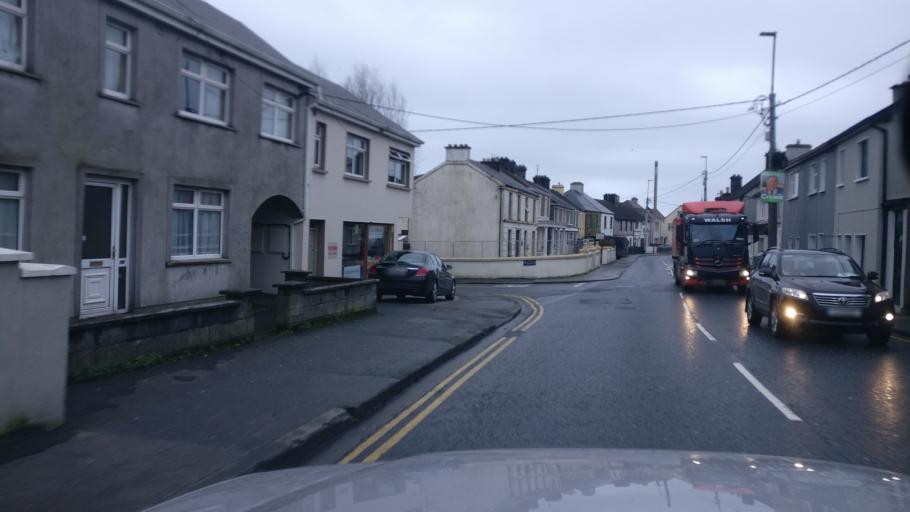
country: IE
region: Connaught
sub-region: County Galway
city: Gaillimh
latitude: 53.2737
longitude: -9.0627
